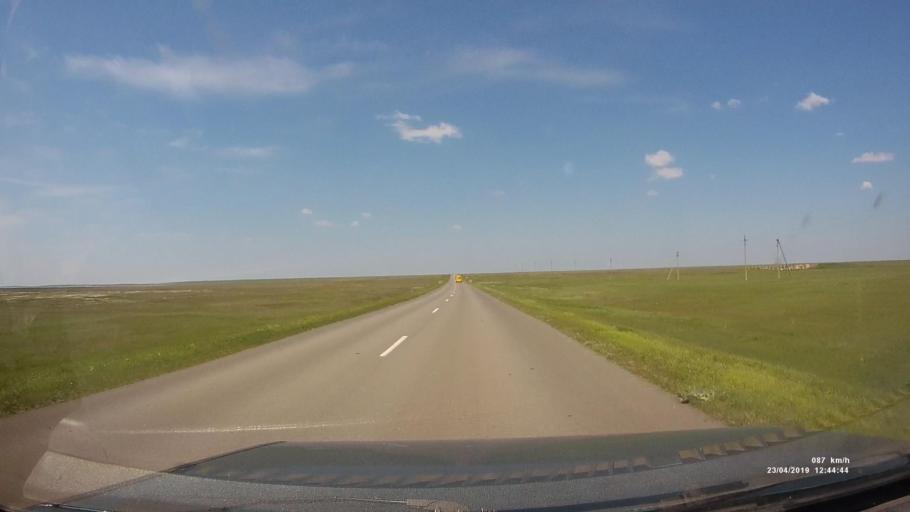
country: RU
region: Kalmykiya
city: Yashalta
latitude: 46.4806
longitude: 42.6458
